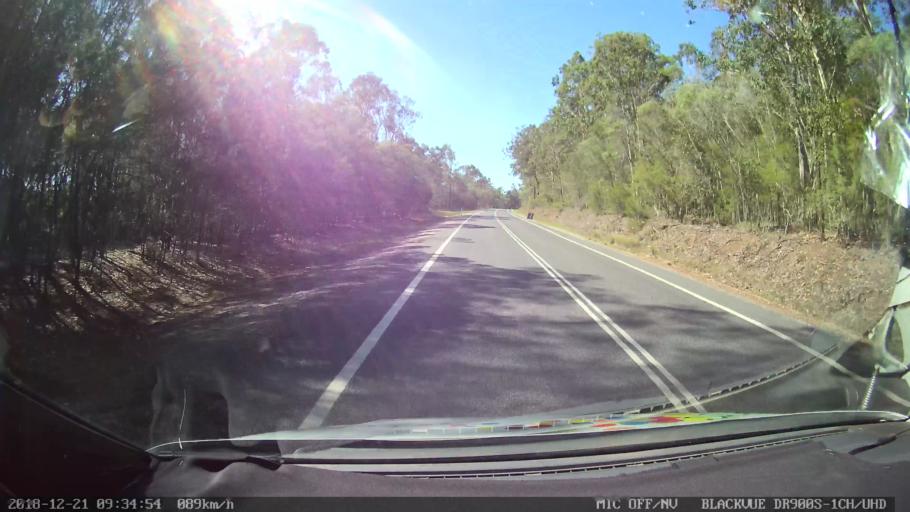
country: AU
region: New South Wales
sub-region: Clarence Valley
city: Grafton
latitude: -29.5037
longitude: 152.9819
